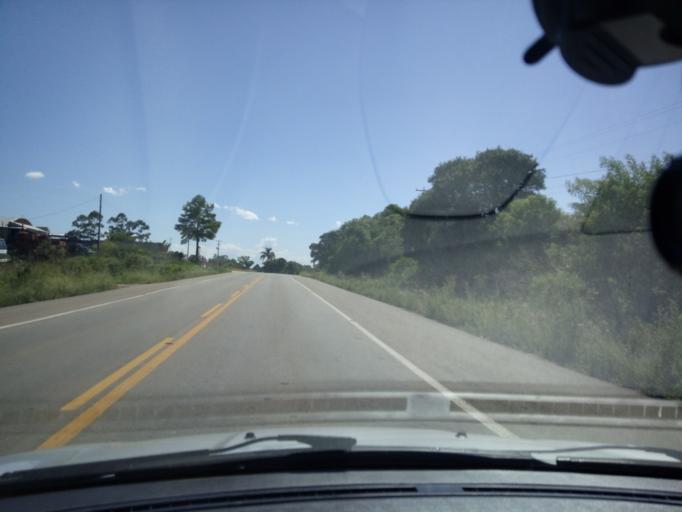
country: BR
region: Rio Grande do Sul
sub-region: Santa Maria
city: Santa Maria
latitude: -29.7329
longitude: -53.5222
